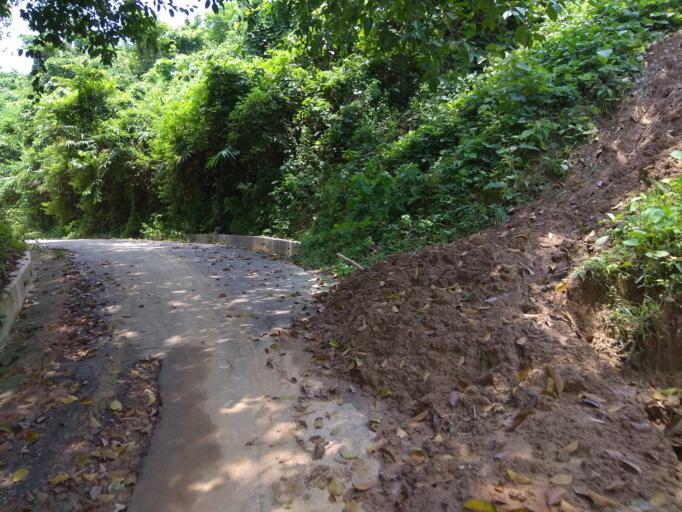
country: BD
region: Chittagong
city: Manikchari
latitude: 22.8941
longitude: 91.9217
